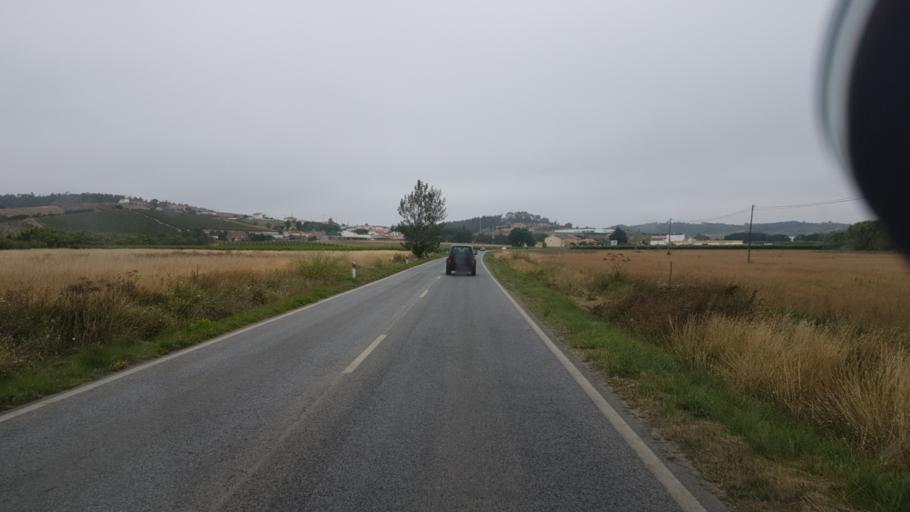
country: PT
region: Lisbon
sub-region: Torres Vedras
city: Torres Vedras
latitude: 39.0930
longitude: -9.2989
